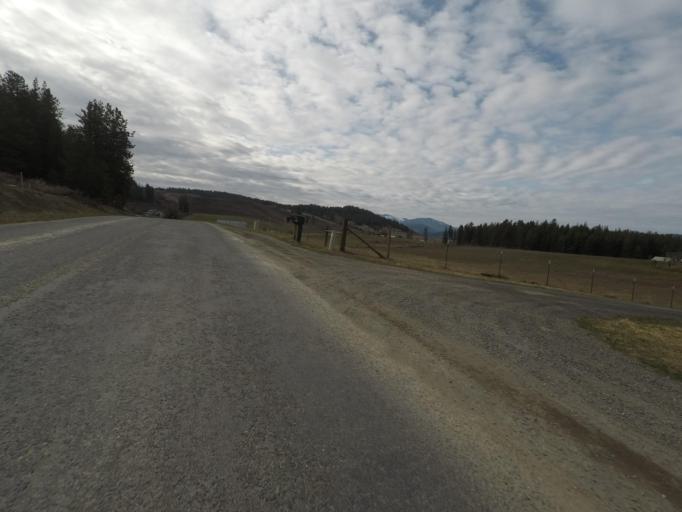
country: US
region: Washington
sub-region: Stevens County
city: Colville
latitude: 48.5230
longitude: -117.8814
